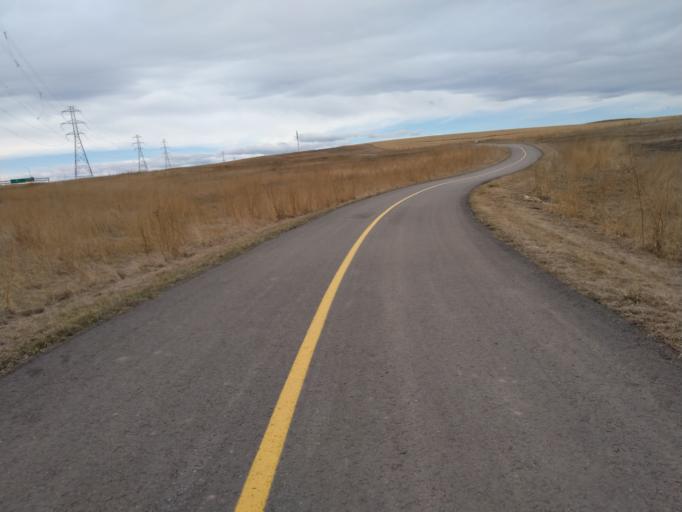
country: CA
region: Alberta
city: Airdrie
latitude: 51.1754
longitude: -114.0526
